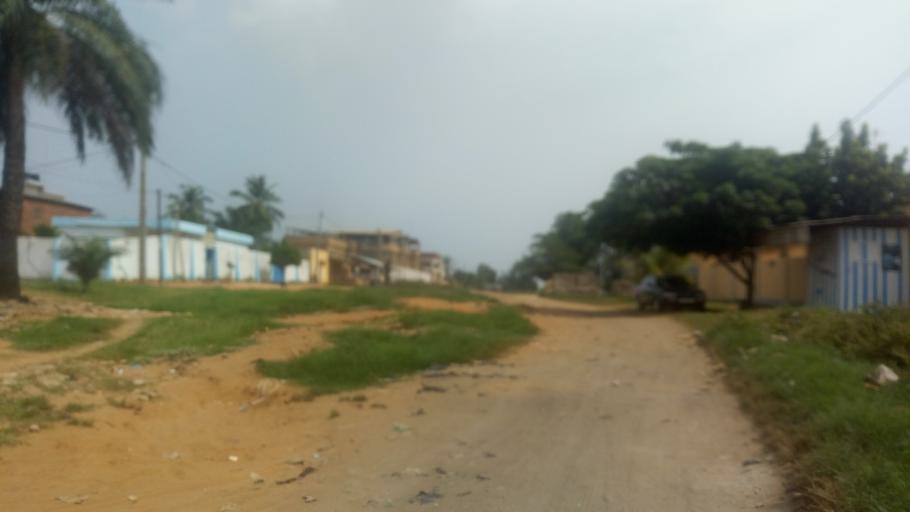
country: TG
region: Maritime
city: Lome
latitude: 6.1751
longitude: 1.1867
